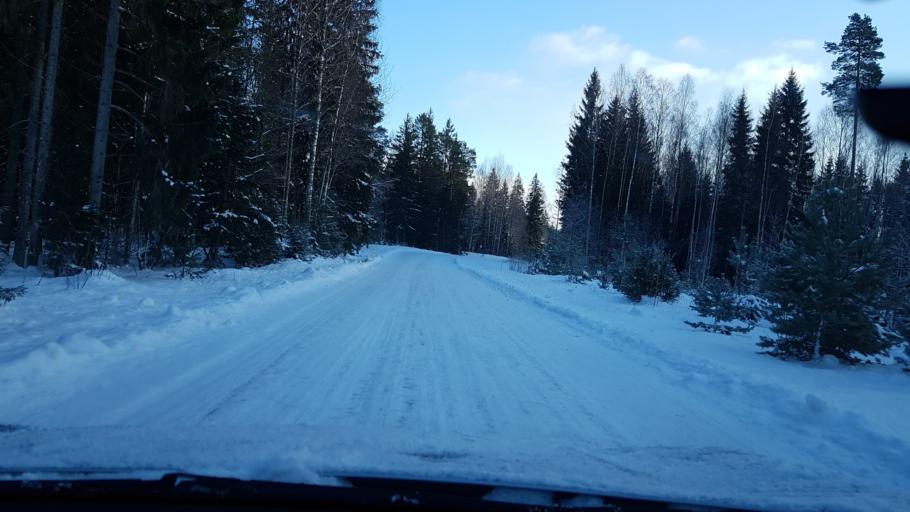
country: EE
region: Harju
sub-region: Nissi vald
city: Turba
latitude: 59.1371
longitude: 24.1873
